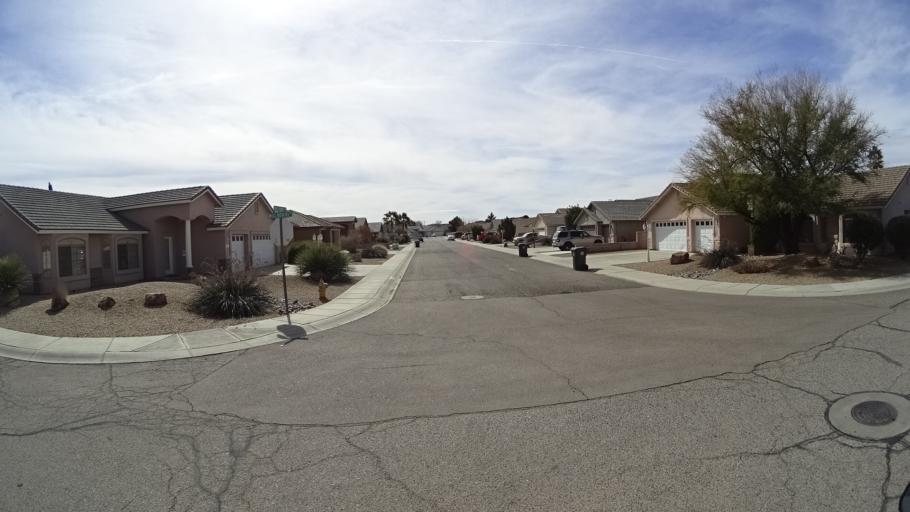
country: US
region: Arizona
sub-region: Mohave County
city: New Kingman-Butler
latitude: 35.2347
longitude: -114.0285
